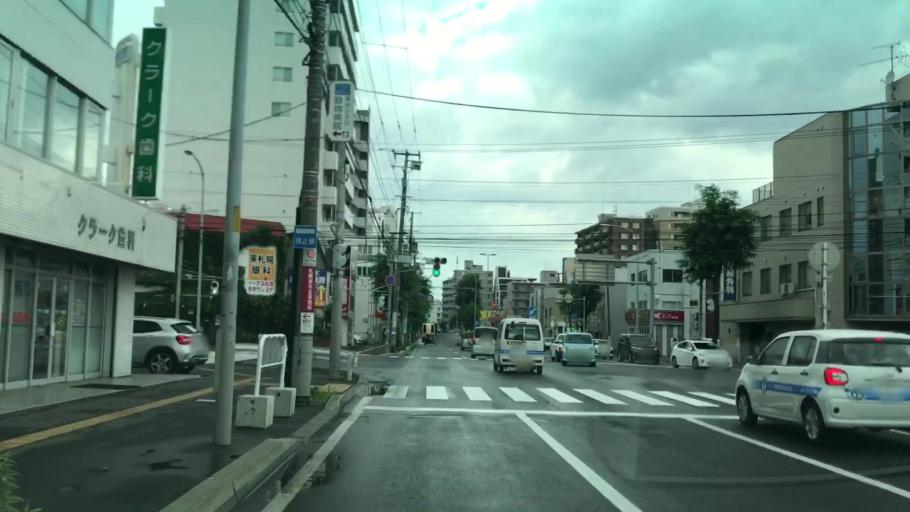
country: JP
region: Hokkaido
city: Sapporo
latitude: 43.0562
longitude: 141.3739
